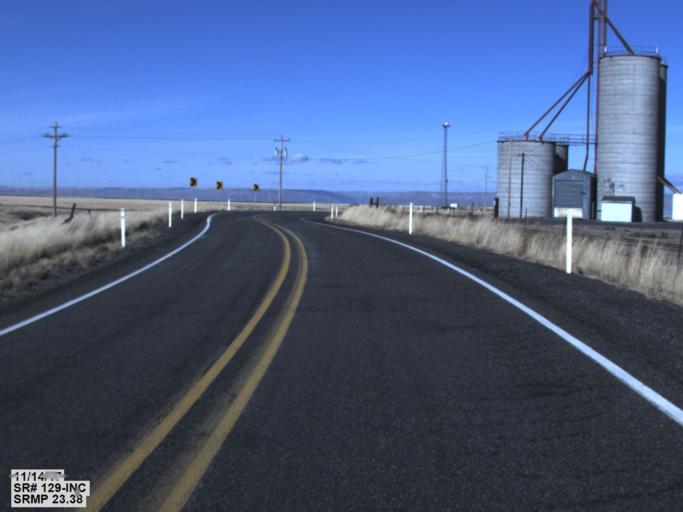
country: US
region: Washington
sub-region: Asotin County
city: Asotin
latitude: 46.2038
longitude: -117.0698
